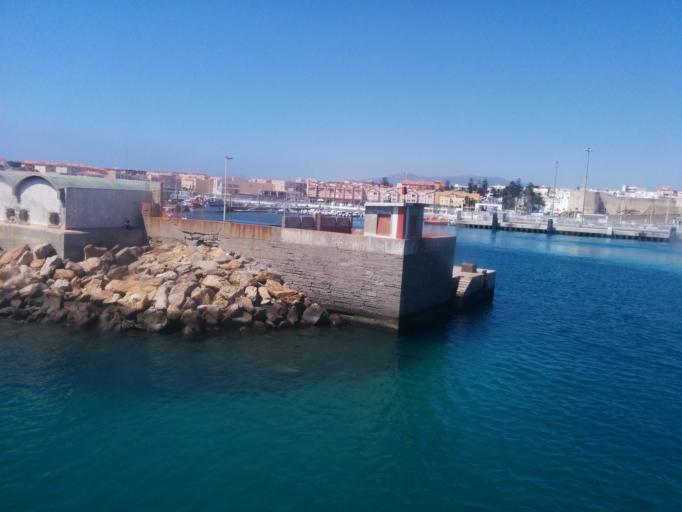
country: ES
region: Andalusia
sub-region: Provincia de Cadiz
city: Tarifa
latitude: 36.0082
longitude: -5.6024
